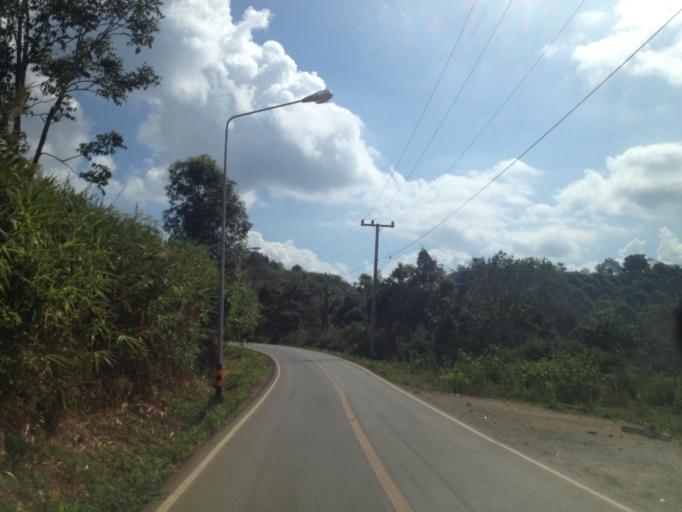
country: TH
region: Mae Hong Son
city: Ban Huai I Huak
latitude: 18.1492
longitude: 98.1344
